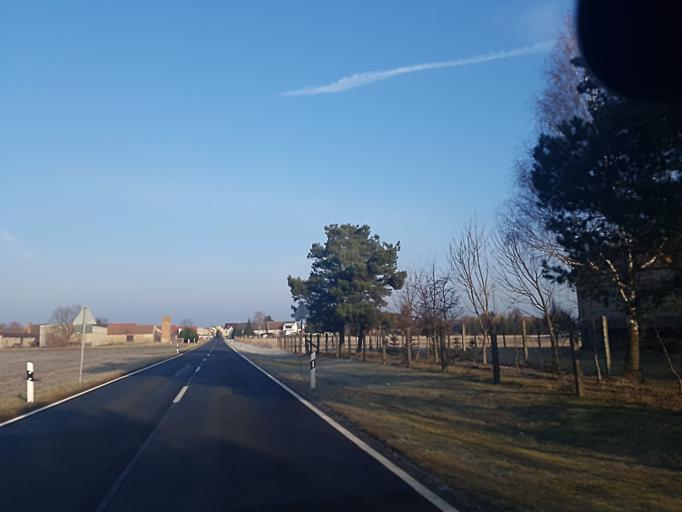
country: DE
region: Brandenburg
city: Golzow
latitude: 52.2434
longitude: 12.6967
